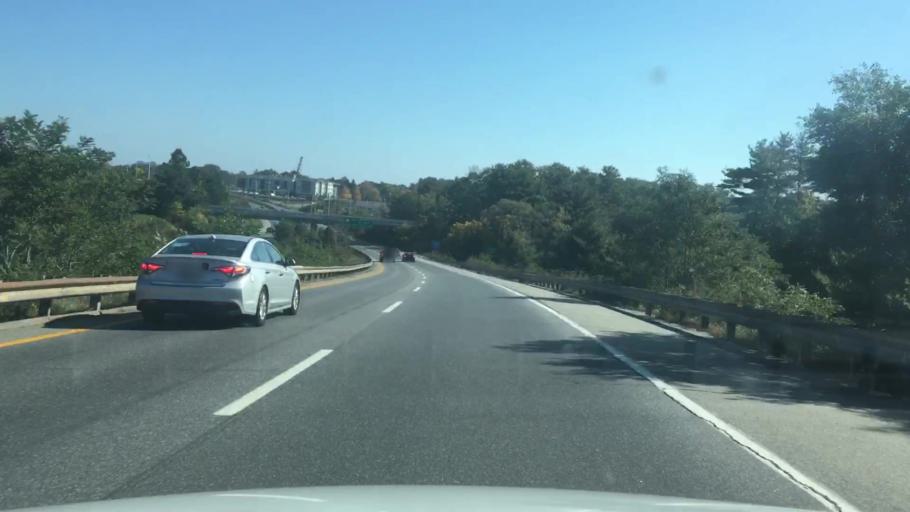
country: US
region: Maine
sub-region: Sagadahoc County
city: Bath
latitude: 43.9071
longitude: -69.8358
